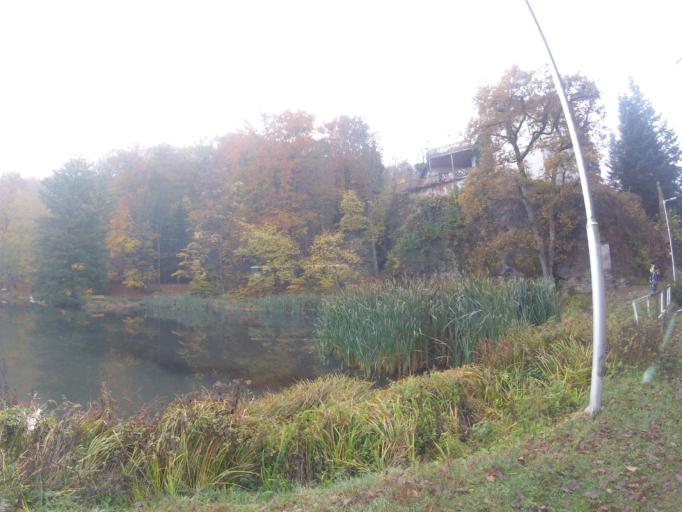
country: HU
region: Borsod-Abauj-Zemplen
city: Tolcsva
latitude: 48.4274
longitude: 21.4411
